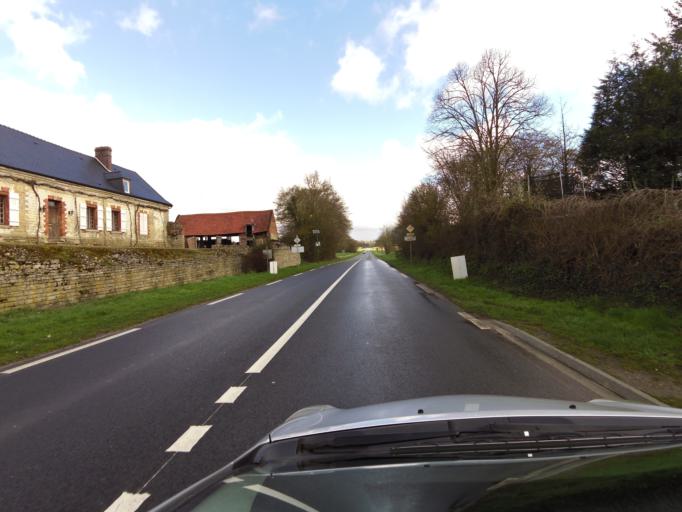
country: FR
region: Picardie
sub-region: Departement de l'Oise
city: Ressons-sur-Matz
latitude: 49.5813
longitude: 2.7100
